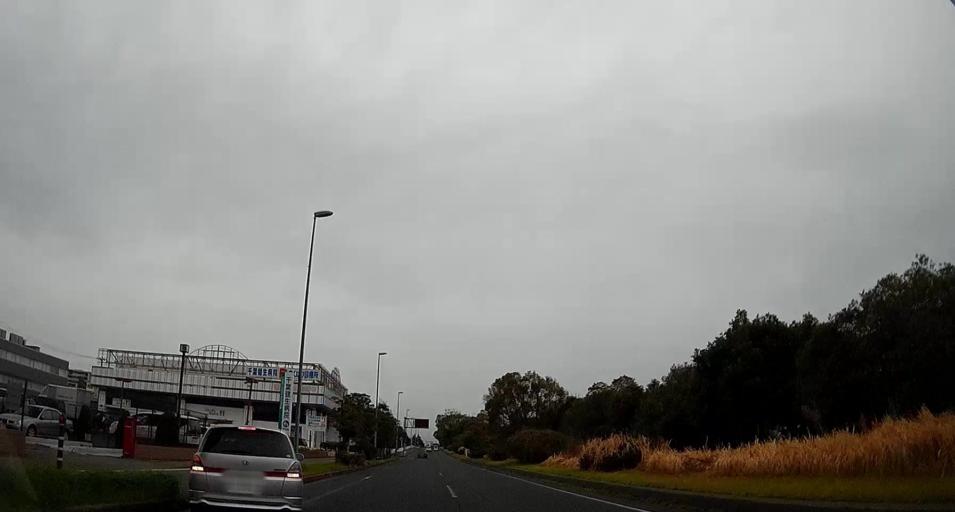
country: JP
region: Chiba
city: Chiba
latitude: 35.6525
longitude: 140.0587
